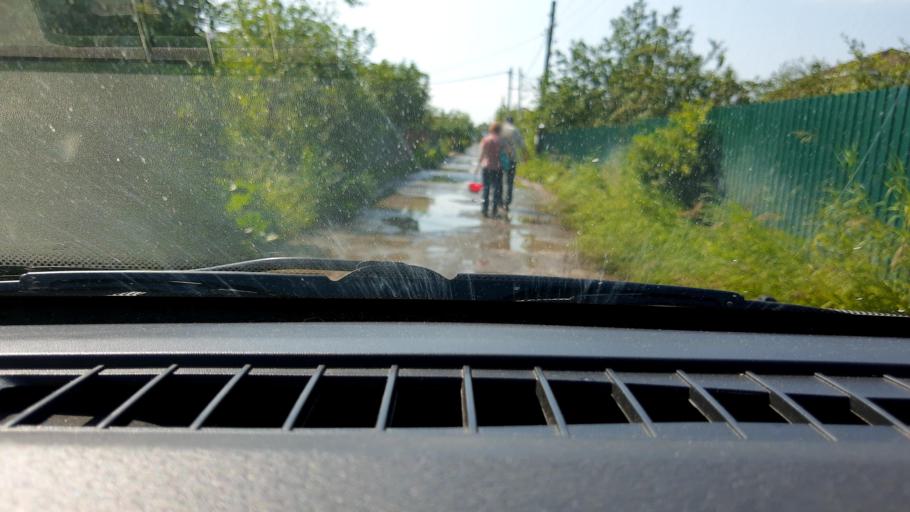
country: RU
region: Nizjnij Novgorod
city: Gorbatovka
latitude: 56.3189
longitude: 43.8286
